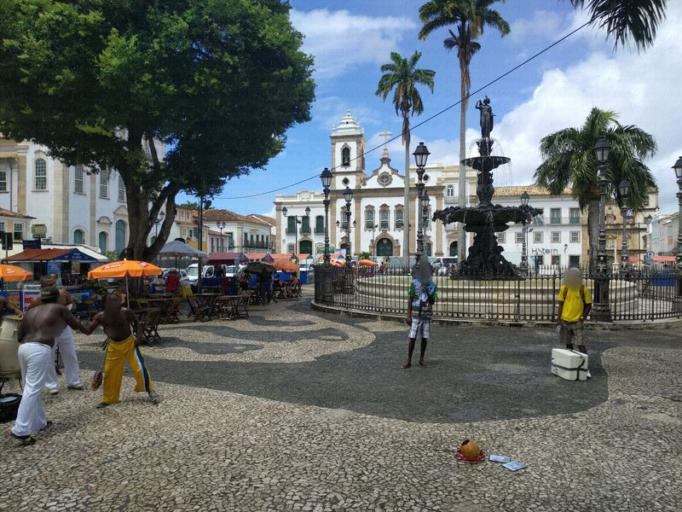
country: BR
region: Bahia
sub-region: Salvador
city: Salvador
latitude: -12.9730
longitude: -38.5100
